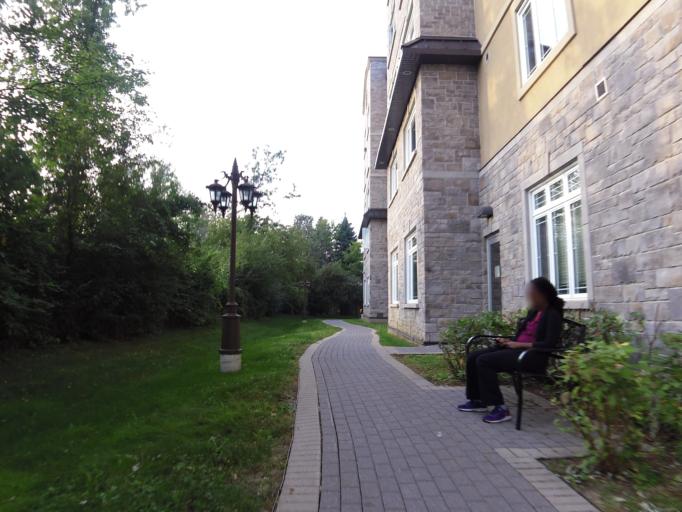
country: CA
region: Ontario
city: Bells Corners
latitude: 45.3326
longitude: -75.8038
